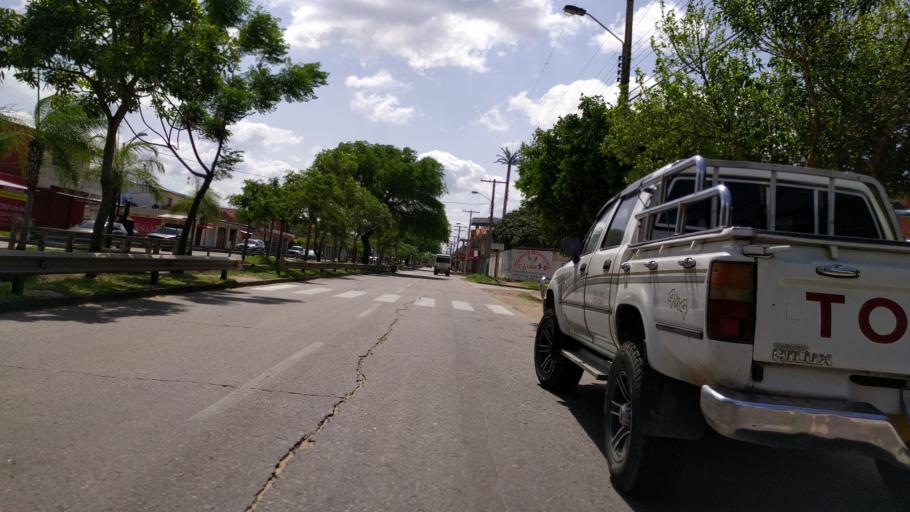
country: BO
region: Santa Cruz
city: Santa Cruz de la Sierra
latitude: -17.7777
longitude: -63.2110
